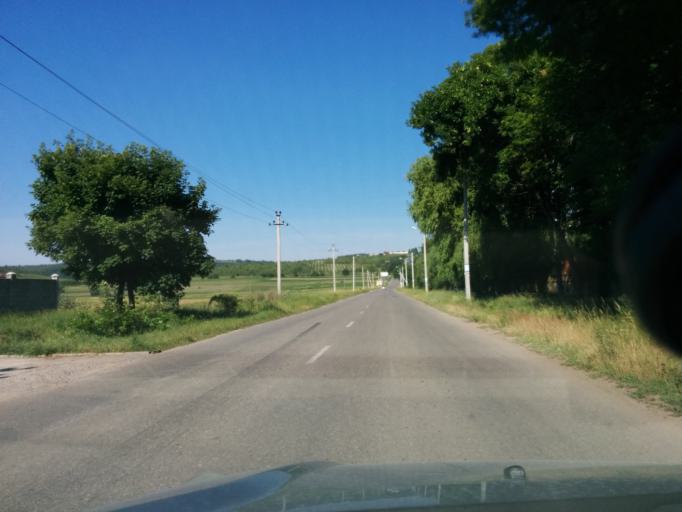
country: MD
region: Chisinau
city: Vadul lui Voda
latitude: 47.0639
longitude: 28.9774
